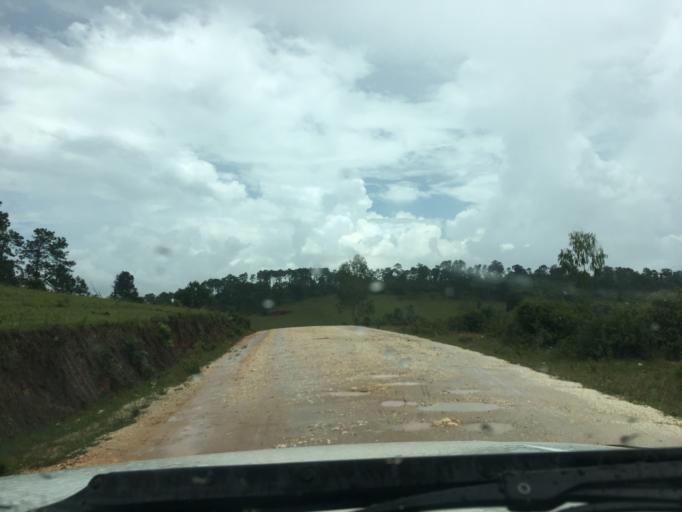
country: LA
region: Xiangkhoang
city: Phonsavan
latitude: 19.6055
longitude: 103.1074
